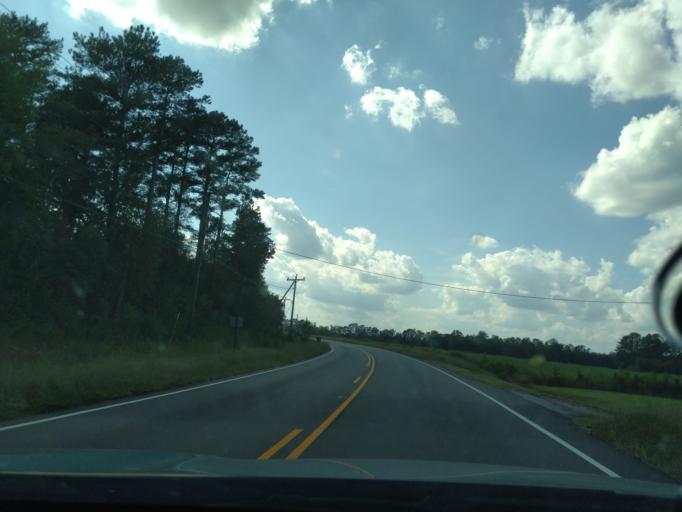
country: US
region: North Carolina
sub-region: Pitt County
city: Bethel
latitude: 35.8251
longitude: -77.3252
